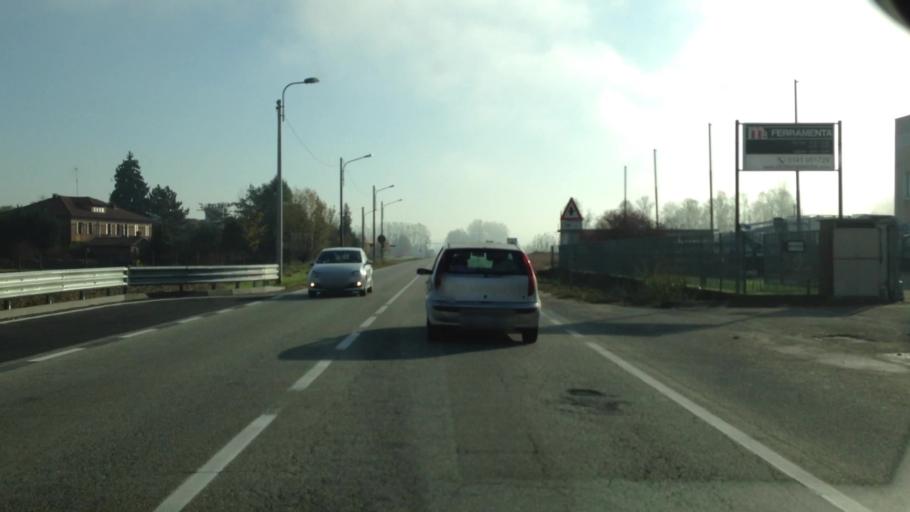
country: IT
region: Piedmont
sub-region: Provincia di Asti
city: Vigliano d'Asti
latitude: 44.8262
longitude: 8.2123
